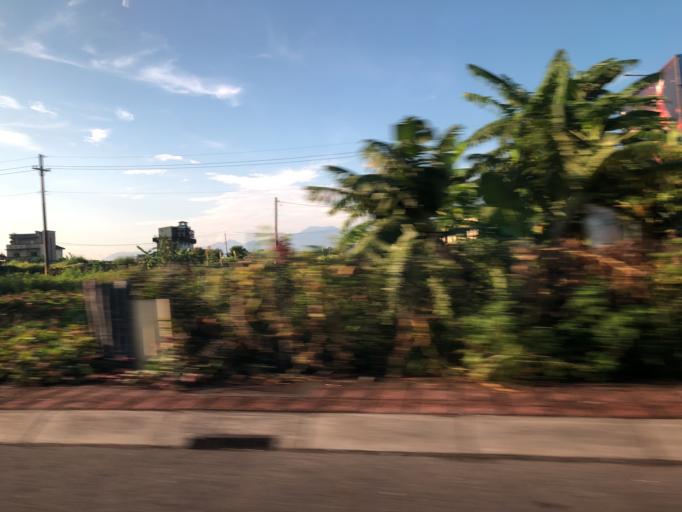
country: TW
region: Taiwan
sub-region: Yilan
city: Yilan
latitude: 24.7499
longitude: 121.7745
